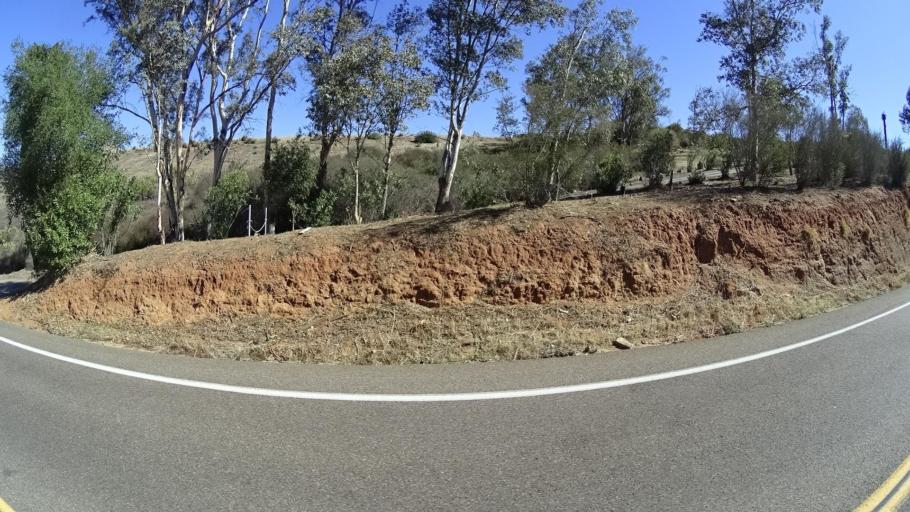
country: US
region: California
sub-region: San Diego County
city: Harbison Canyon
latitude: 32.8454
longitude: -116.8047
